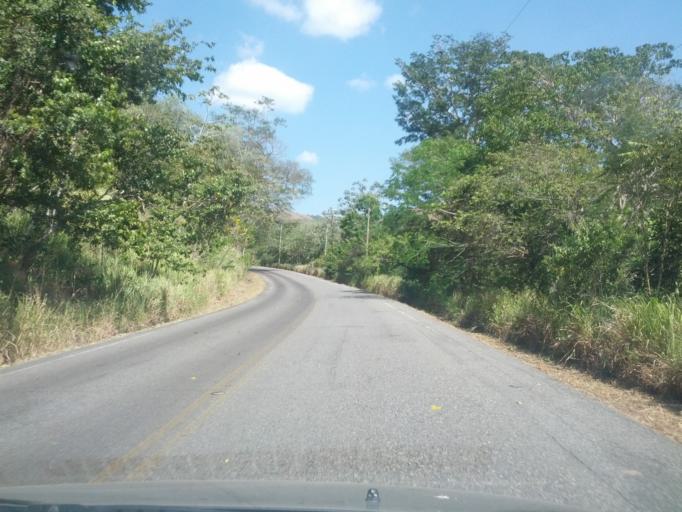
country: CR
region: Puntarenas
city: Buenos Aires
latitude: 8.9607
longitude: -83.3090
